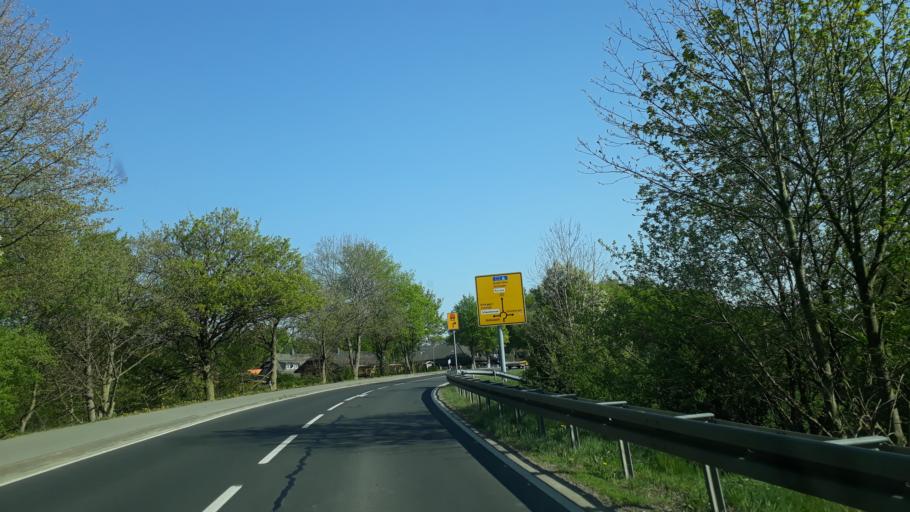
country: DE
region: North Rhine-Westphalia
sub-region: Regierungsbezirk Koln
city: Simmerath
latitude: 50.6233
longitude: 6.3230
